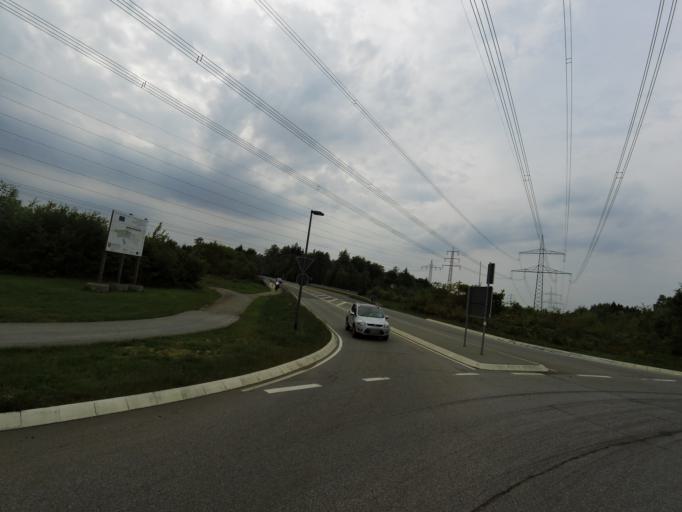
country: DE
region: Rheinland-Pfalz
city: Dorth
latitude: 50.1588
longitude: 7.5780
